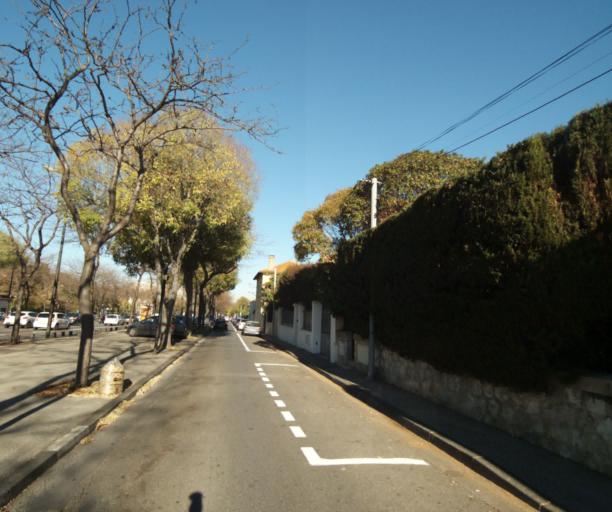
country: FR
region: Provence-Alpes-Cote d'Azur
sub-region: Departement des Bouches-du-Rhone
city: Marseille 09
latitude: 43.2558
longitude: 5.4010
